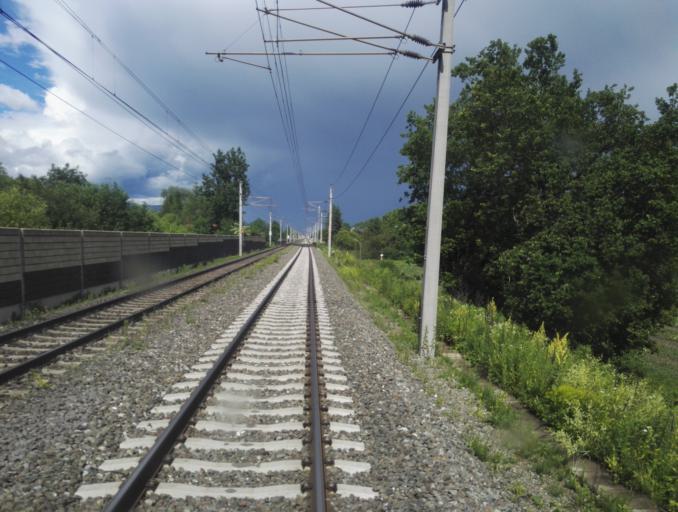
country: AT
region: Styria
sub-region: Politischer Bezirk Bruck-Muerzzuschlag
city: Frauenberg
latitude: 47.4530
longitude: 15.3252
